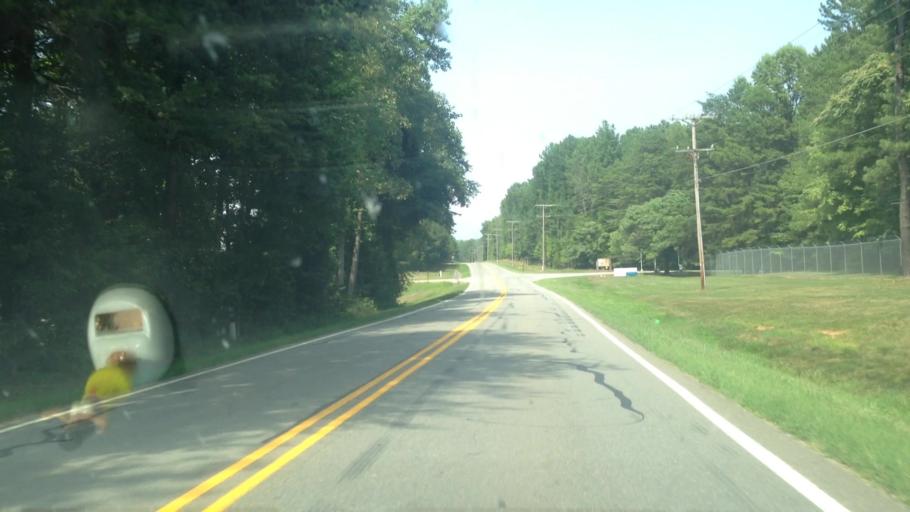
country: US
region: North Carolina
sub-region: Stokes County
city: Walnut Cove
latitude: 36.2889
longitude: -80.0663
